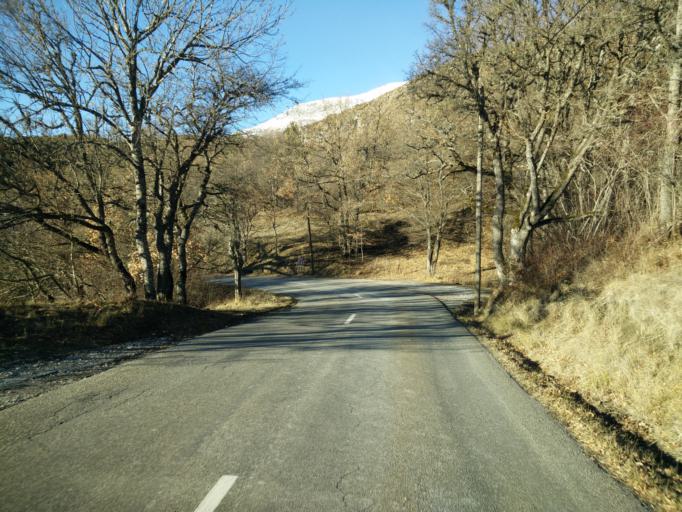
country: FR
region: Provence-Alpes-Cote d'Azur
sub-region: Departement des Alpes-de-Haute-Provence
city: Castellane
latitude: 43.7958
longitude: 6.3867
